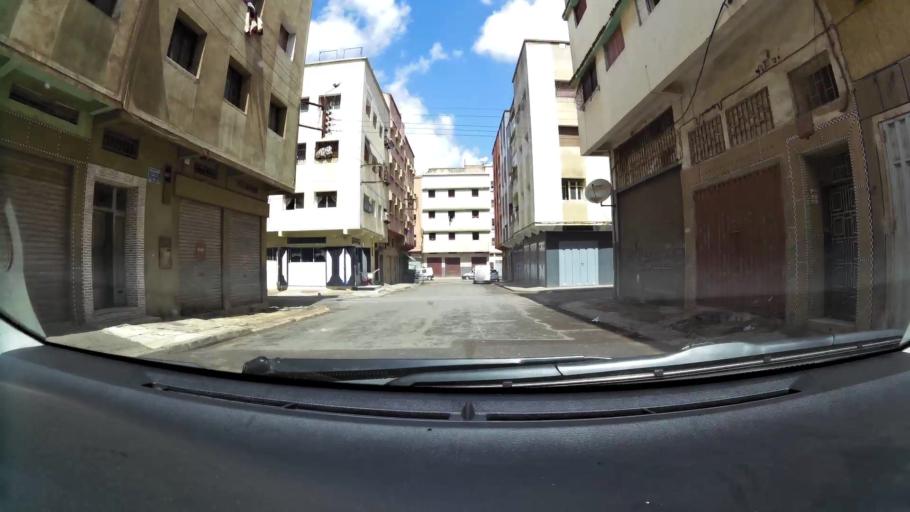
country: MA
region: Grand Casablanca
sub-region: Casablanca
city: Casablanca
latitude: 33.5375
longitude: -7.5705
